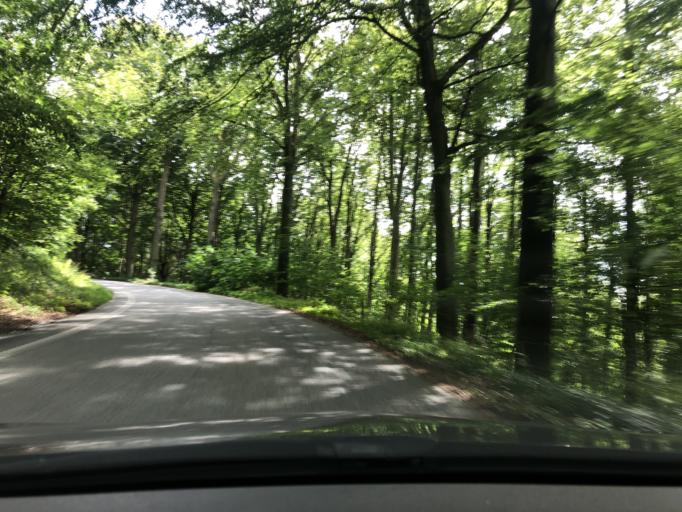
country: DK
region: South Denmark
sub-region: Vejle Kommune
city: Jelling
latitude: 55.6996
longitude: 9.4424
